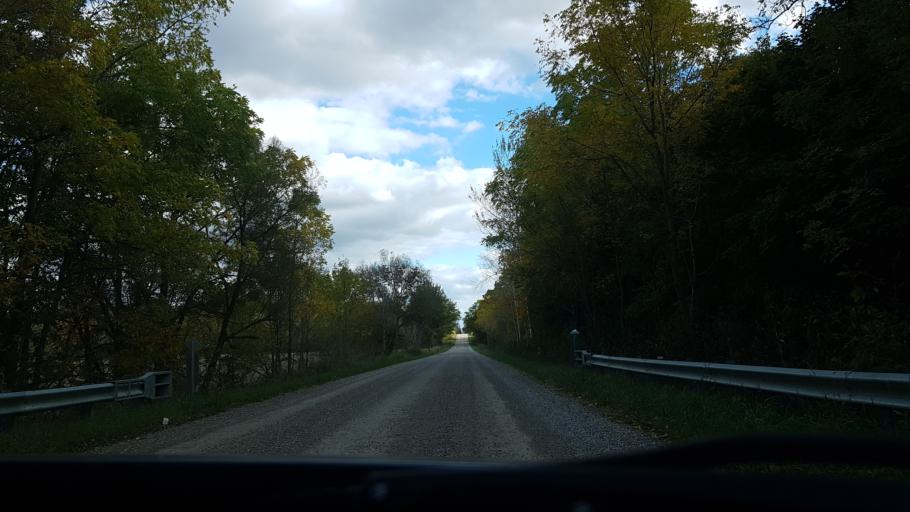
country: CA
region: Ontario
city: South Huron
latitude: 43.0948
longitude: -81.5928
